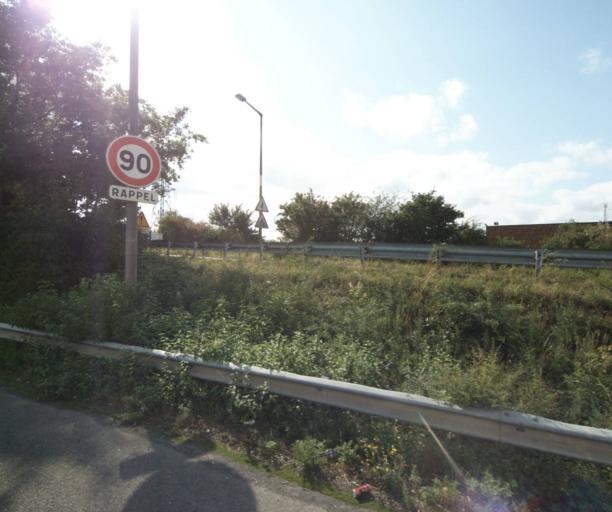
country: FR
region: Nord-Pas-de-Calais
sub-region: Departement du Nord
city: Lys-lez-Lannoy
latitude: 50.6805
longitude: 3.2258
